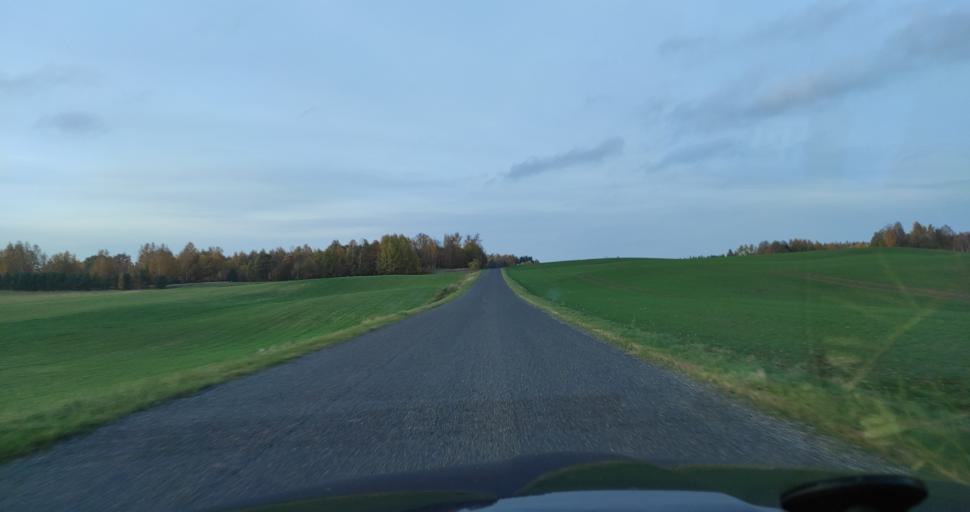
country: LV
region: Aizpute
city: Aizpute
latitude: 56.7039
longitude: 21.7943
